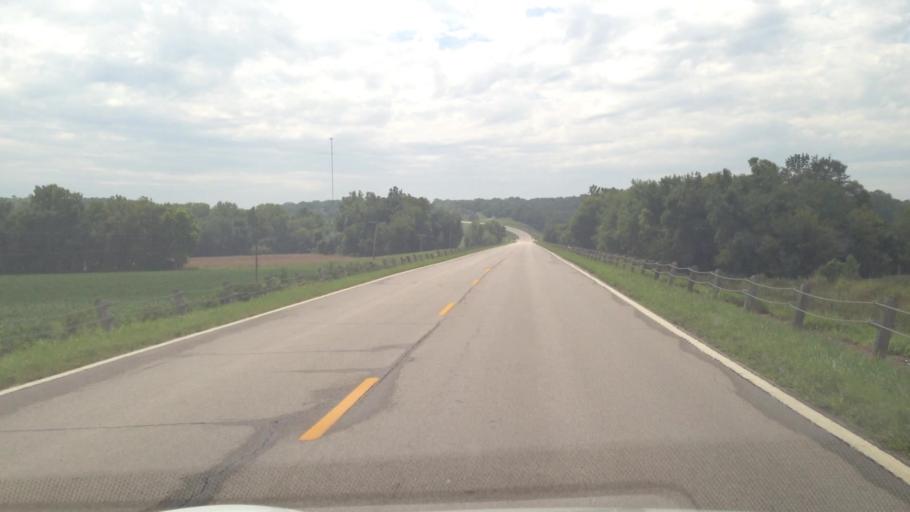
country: US
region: Kansas
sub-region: Bourbon County
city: Fort Scott
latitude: 37.8397
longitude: -94.9812
